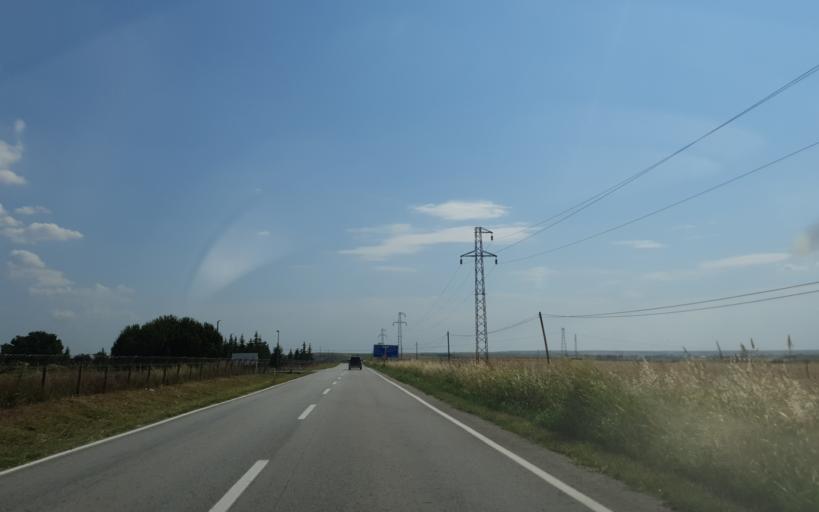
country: TR
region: Kirklareli
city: Buyukkaristiran
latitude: 41.3121
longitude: 27.5170
